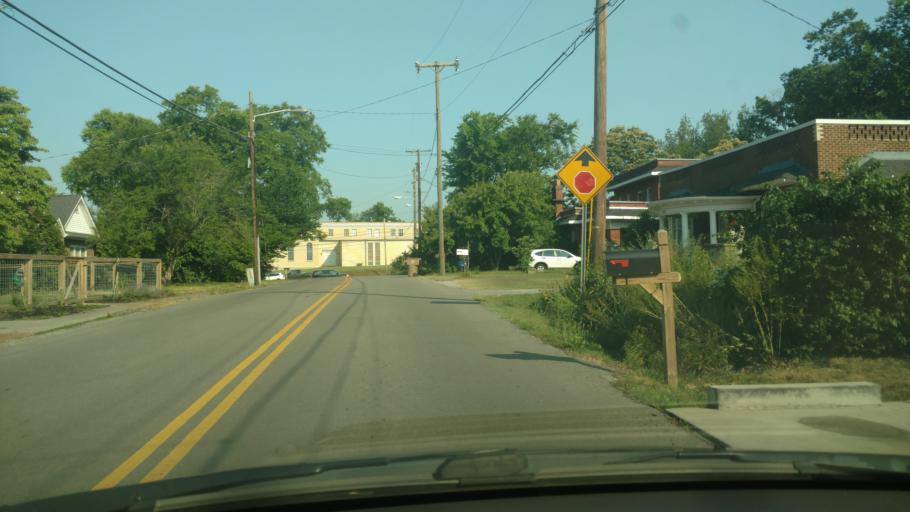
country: US
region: Tennessee
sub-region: Davidson County
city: Nashville
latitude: 36.2207
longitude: -86.7256
